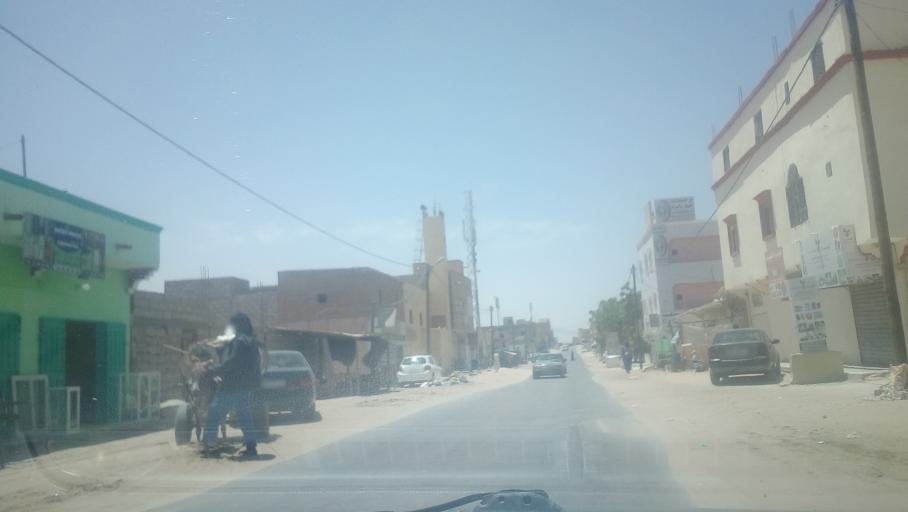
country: MR
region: Nouakchott
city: Nouakchott
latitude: 18.0633
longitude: -15.9596
